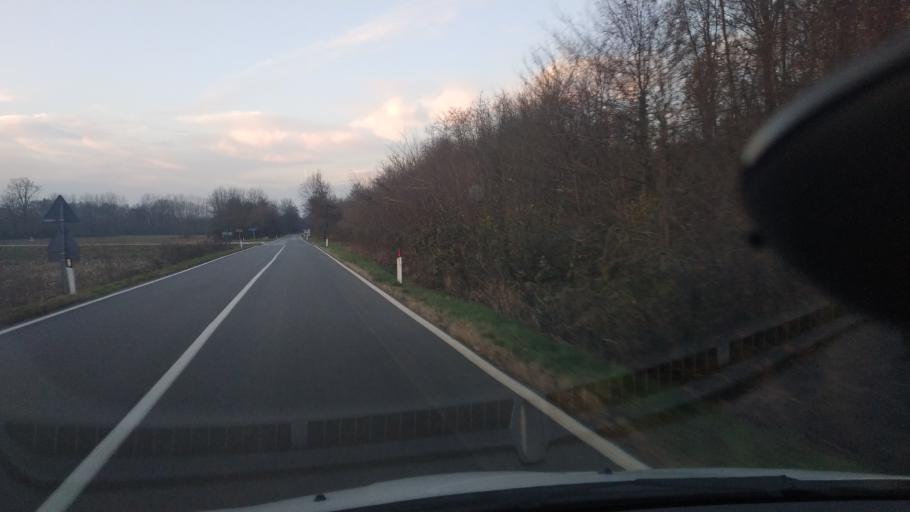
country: IT
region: Piedmont
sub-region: Provincia di Torino
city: Montanaro
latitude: 45.2477
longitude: 7.8411
